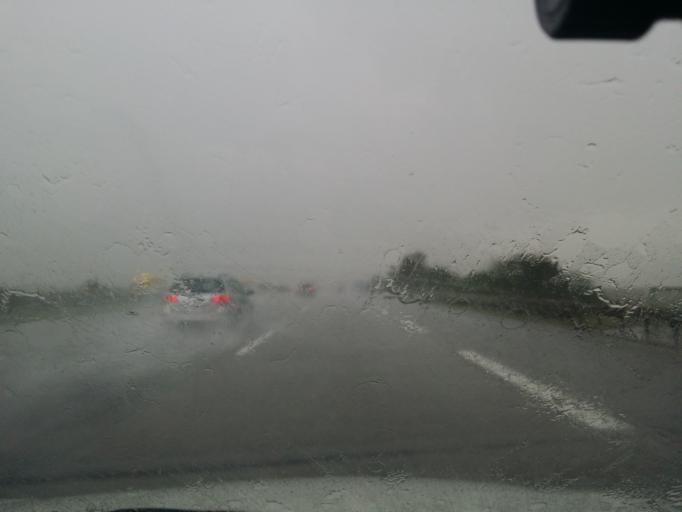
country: DE
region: Thuringia
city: Troistedt
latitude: 50.9497
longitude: 11.2419
